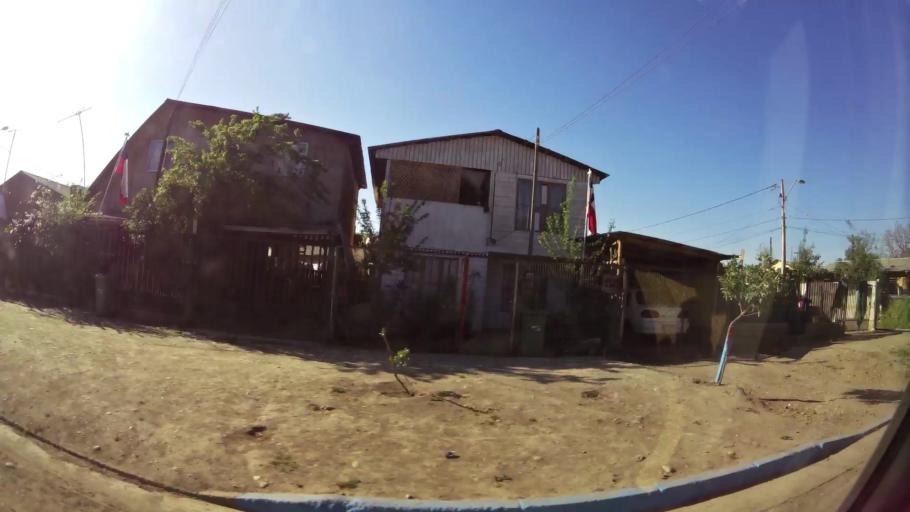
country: CL
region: Santiago Metropolitan
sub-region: Provincia de Talagante
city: Penaflor
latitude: -33.6160
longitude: -70.8710
